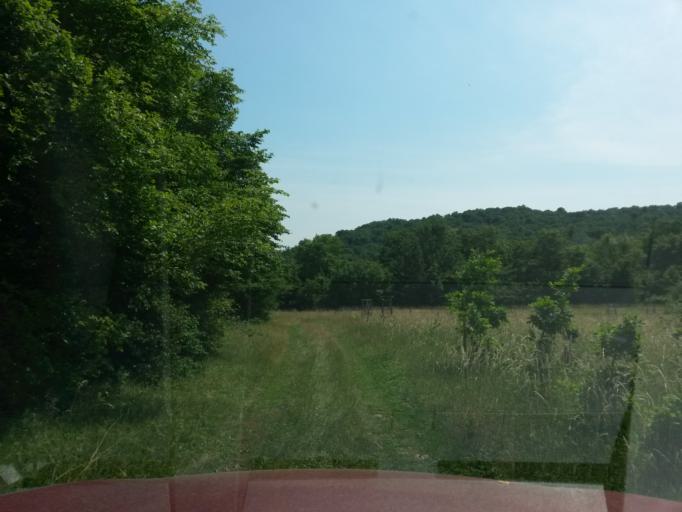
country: SK
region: Kosicky
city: Moldava nad Bodvou
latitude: 48.6448
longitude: 20.9525
